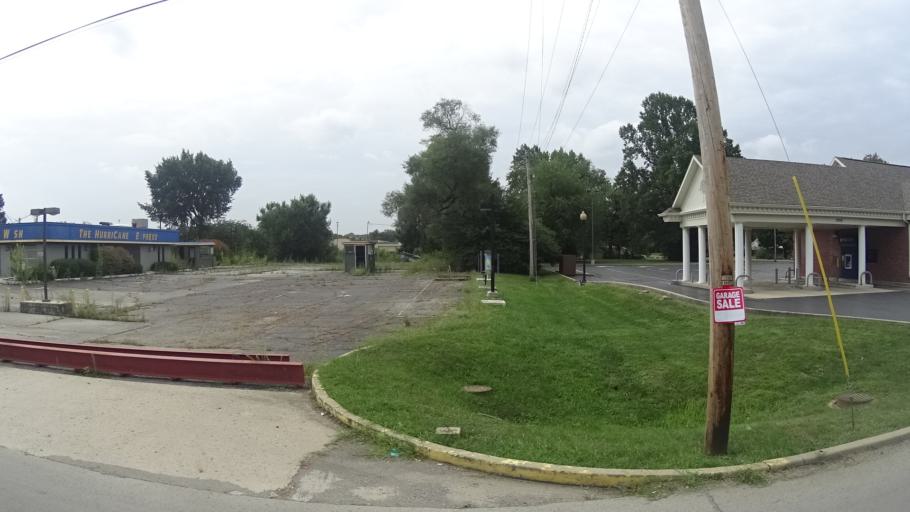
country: US
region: Indiana
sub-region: Madison County
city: Edgewood
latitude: 40.1015
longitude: -85.7206
